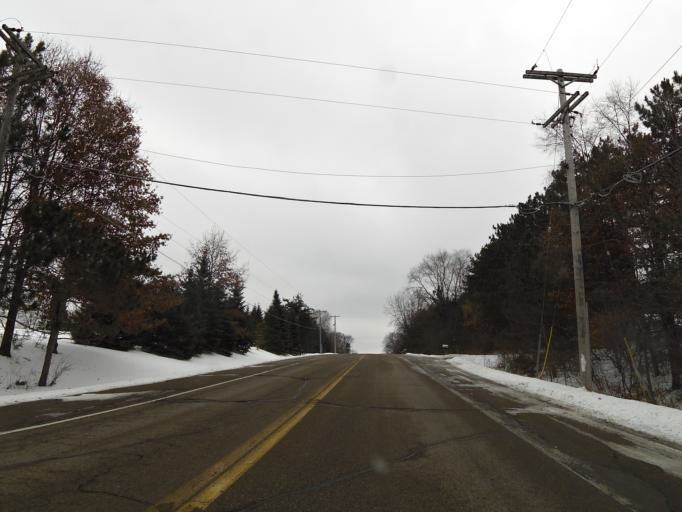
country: US
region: Minnesota
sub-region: Washington County
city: Oak Park Heights
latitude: 45.0036
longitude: -92.8226
